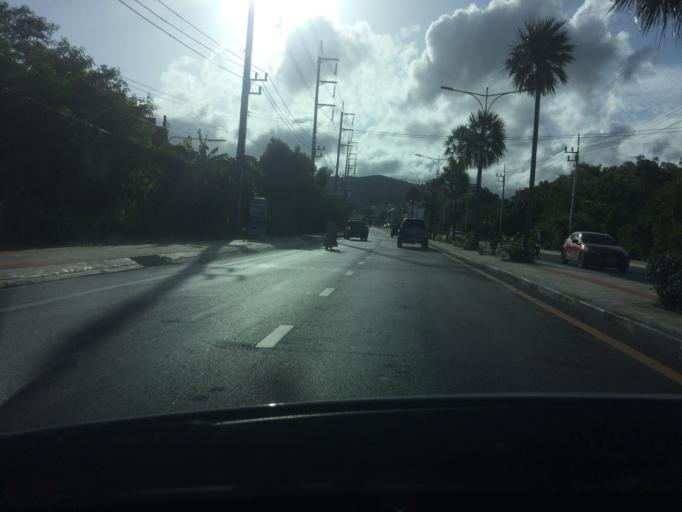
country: TH
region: Phuket
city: Mueang Phuket
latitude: 7.8715
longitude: 98.3703
